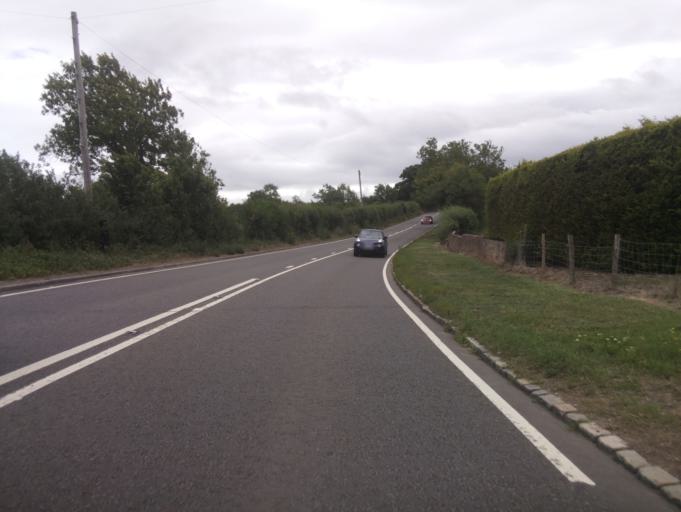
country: GB
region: England
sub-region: Gloucestershire
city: Tewkesbury
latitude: 52.0136
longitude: -2.1625
